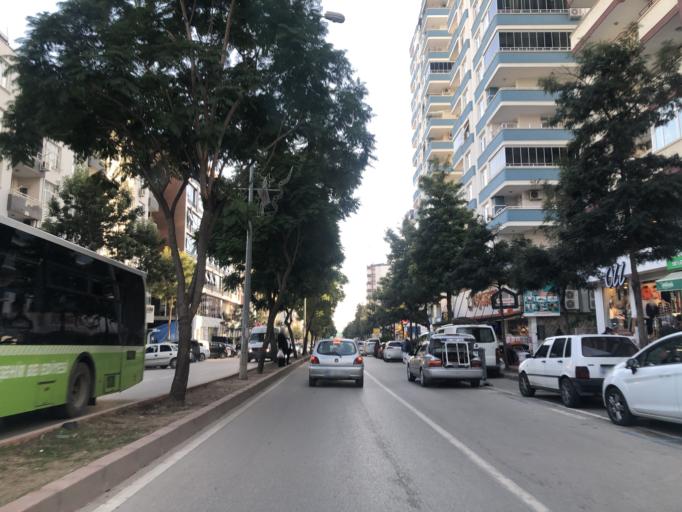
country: TR
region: Adana
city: Adana
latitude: 37.0405
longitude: 35.3040
